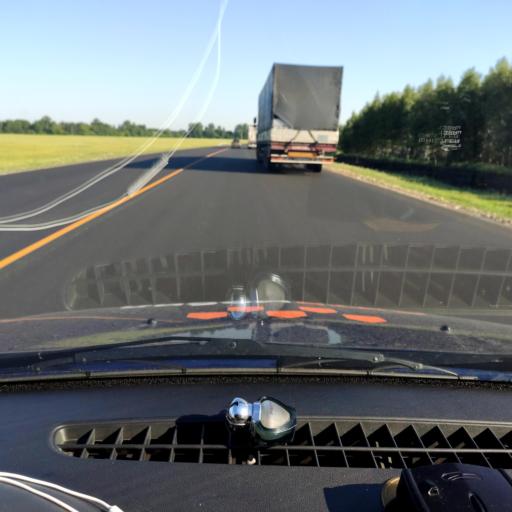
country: RU
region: Orjol
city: Zmiyevka
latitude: 52.7315
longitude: 36.3239
